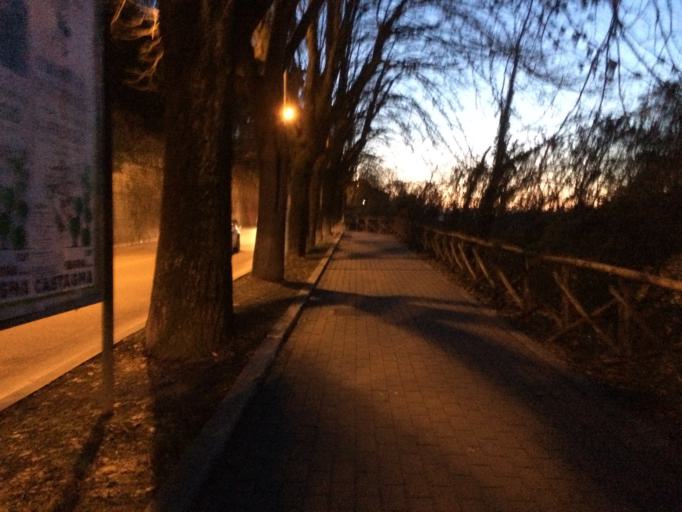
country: IT
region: Umbria
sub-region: Provincia di Perugia
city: Perugia
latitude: 43.1149
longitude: 12.3831
